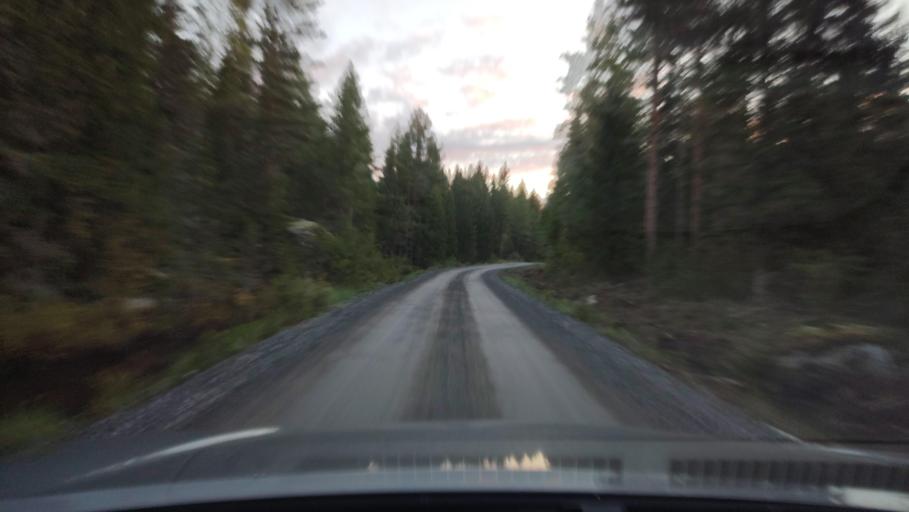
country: FI
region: Ostrobothnia
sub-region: Sydosterbotten
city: Kristinestad
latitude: 62.1921
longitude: 21.5425
